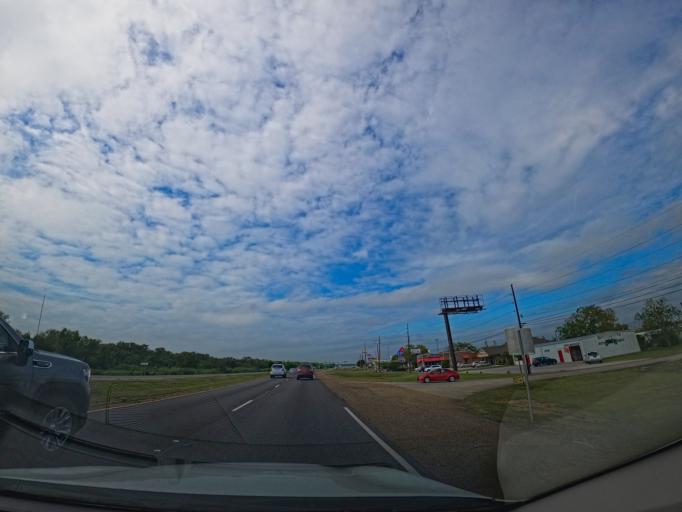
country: US
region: Louisiana
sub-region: Saint Mary Parish
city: Bayou Vista
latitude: 29.6837
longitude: -91.2586
